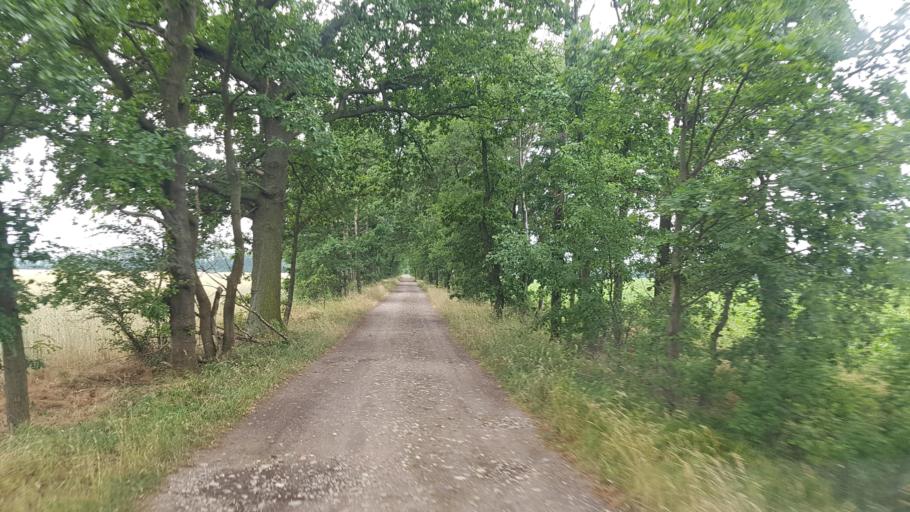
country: DE
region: Brandenburg
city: Schraden
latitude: 51.4185
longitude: 13.6814
